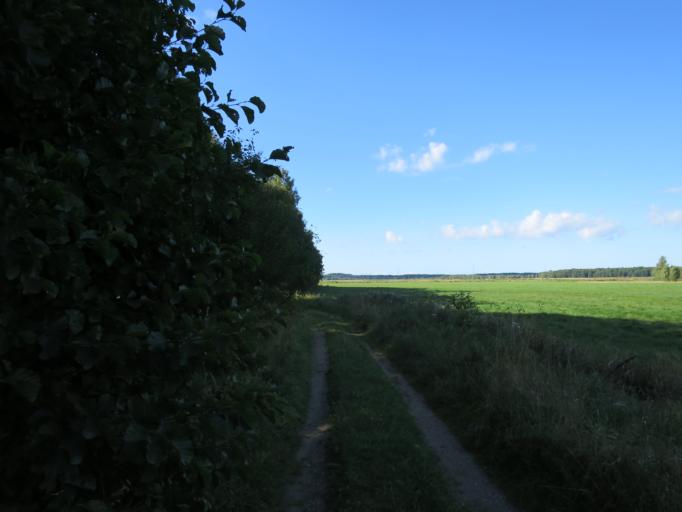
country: LV
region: Riga
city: Jaunciems
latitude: 57.0790
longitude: 24.2099
